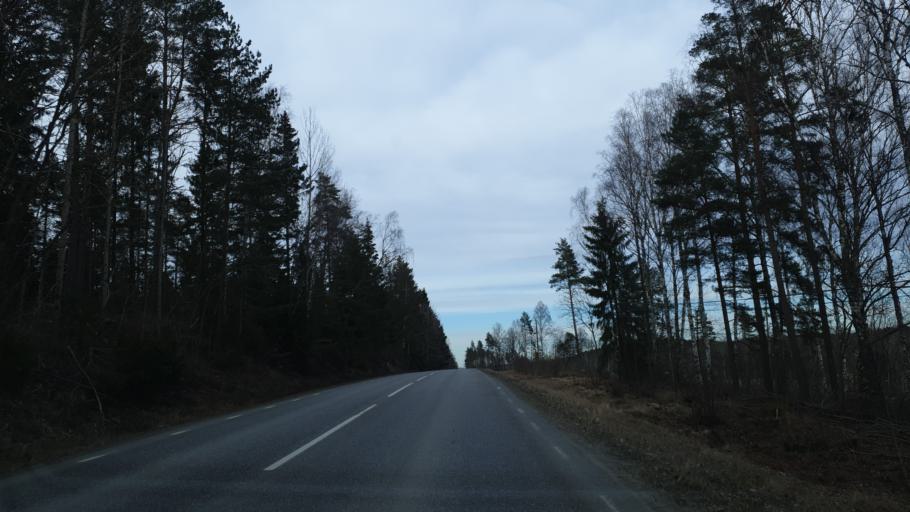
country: SE
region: Stockholm
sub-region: Osterakers Kommun
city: Akersberga
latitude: 59.5882
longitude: 18.2969
